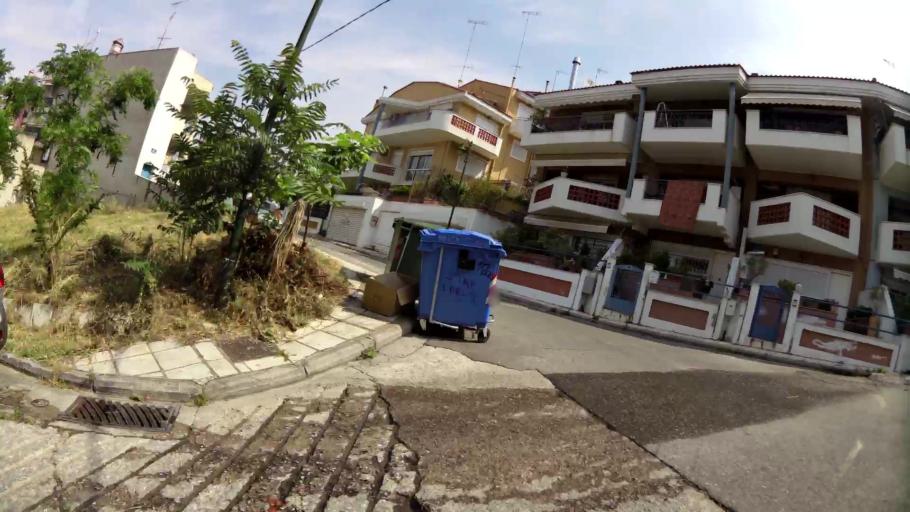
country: GR
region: Central Macedonia
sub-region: Nomos Thessalonikis
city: Agios Pavlos
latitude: 40.6448
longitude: 22.9563
